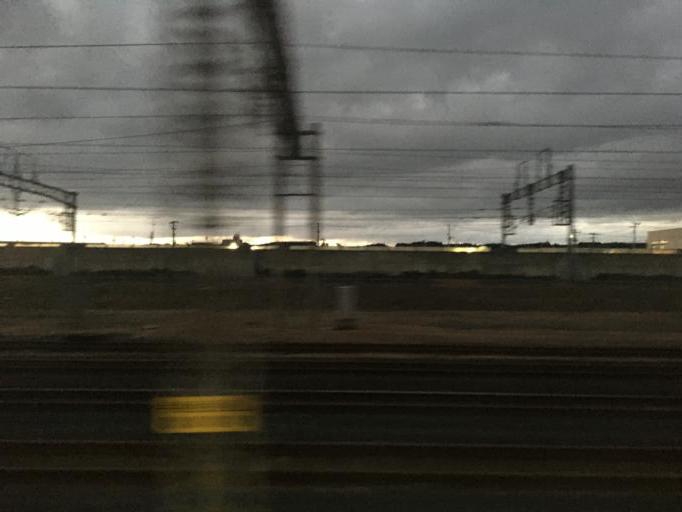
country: JP
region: Aomori
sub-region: Hachinohe Shi
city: Uchimaru
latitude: 40.5108
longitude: 141.4330
